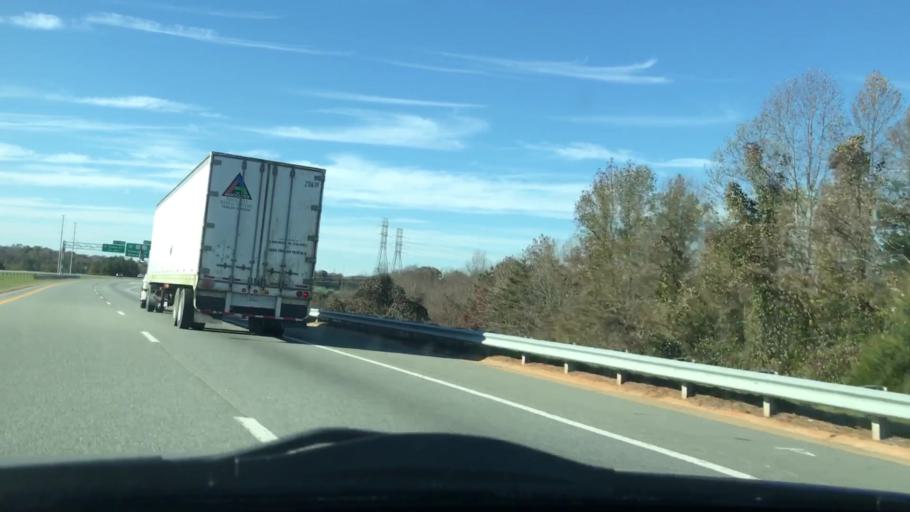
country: US
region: North Carolina
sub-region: Randolph County
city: Archdale
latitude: 35.9413
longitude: -79.9661
